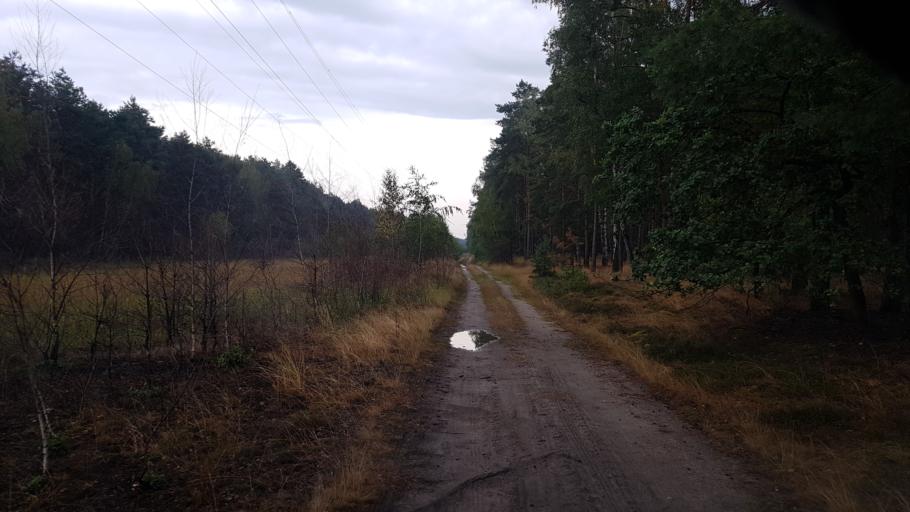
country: DE
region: Brandenburg
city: Finsterwalde
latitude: 51.6396
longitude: 13.7711
